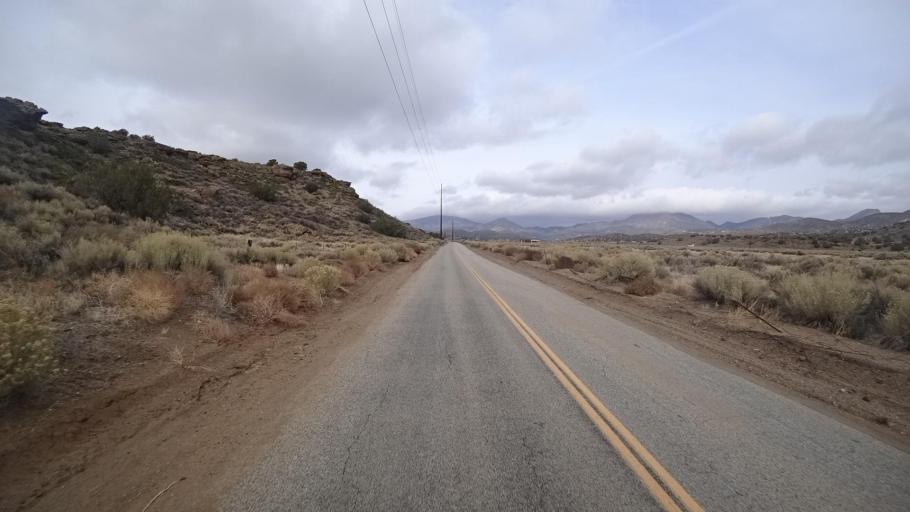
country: US
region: California
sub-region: Kern County
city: Tehachapi
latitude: 35.1589
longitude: -118.3234
